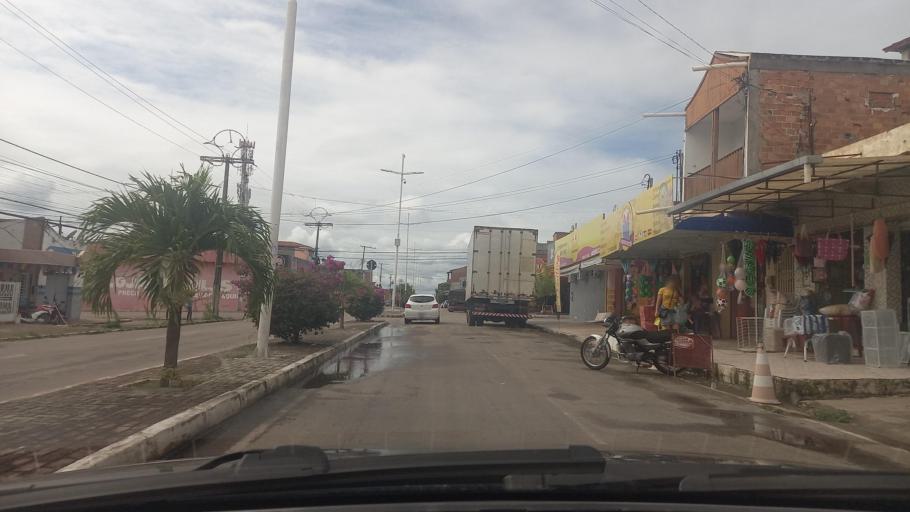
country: BR
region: Bahia
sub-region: Paulo Afonso
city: Paulo Afonso
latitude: -9.4412
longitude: -38.2141
